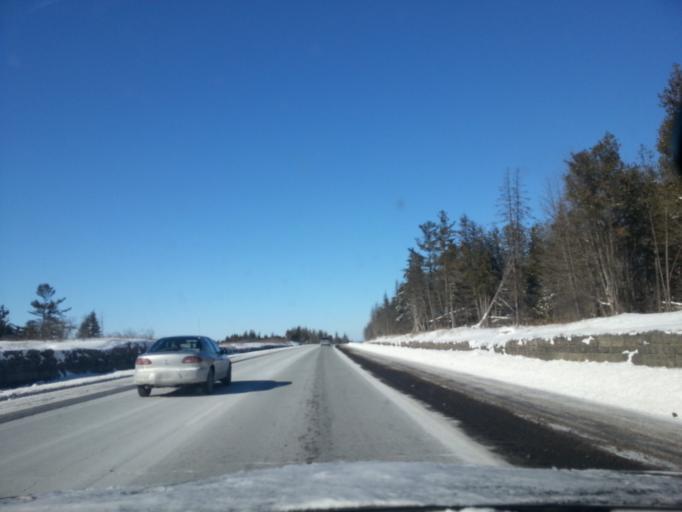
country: CA
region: Ontario
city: Arnprior
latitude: 45.3393
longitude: -76.1871
